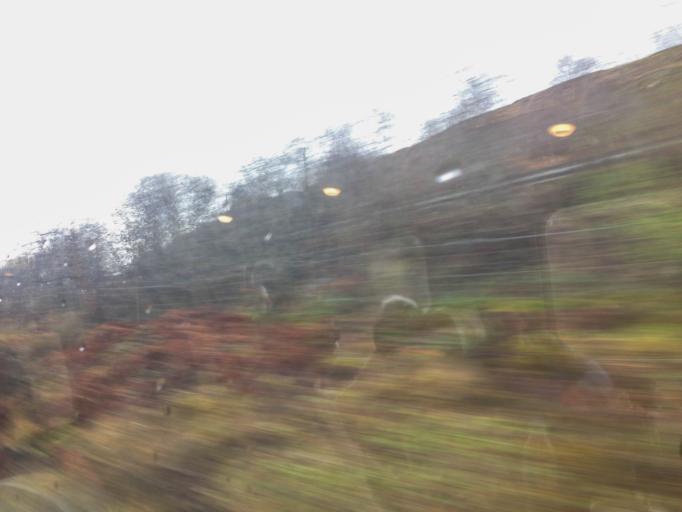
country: GB
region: Scotland
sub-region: Argyll and Bute
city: Isle Of Mull
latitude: 56.9892
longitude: -5.8254
